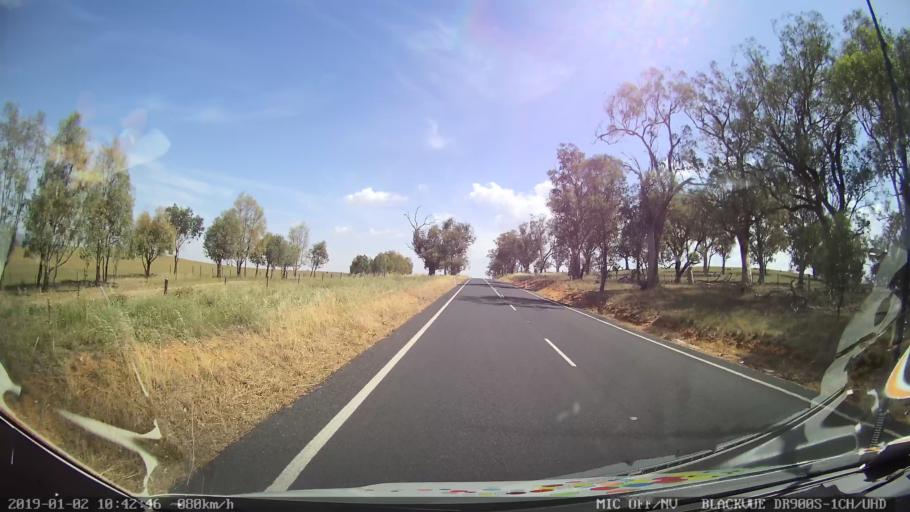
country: AU
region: New South Wales
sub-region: Cootamundra
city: Cootamundra
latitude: -34.7803
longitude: 148.3065
